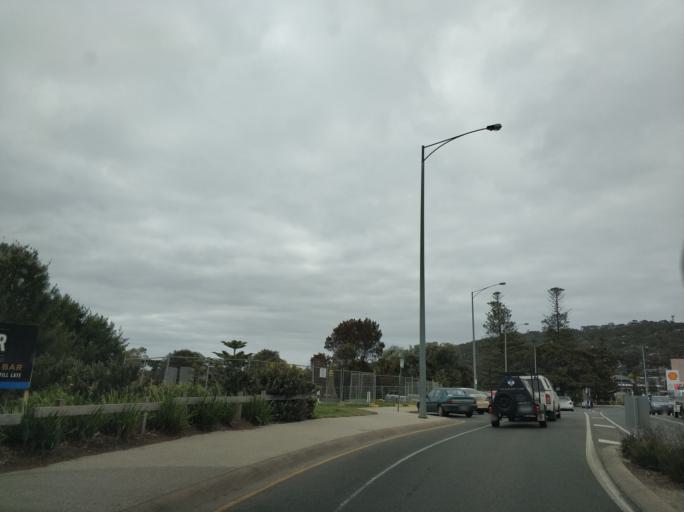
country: AU
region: Victoria
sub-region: Surf Coast
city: Anglesea
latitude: -38.5378
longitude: 143.9751
